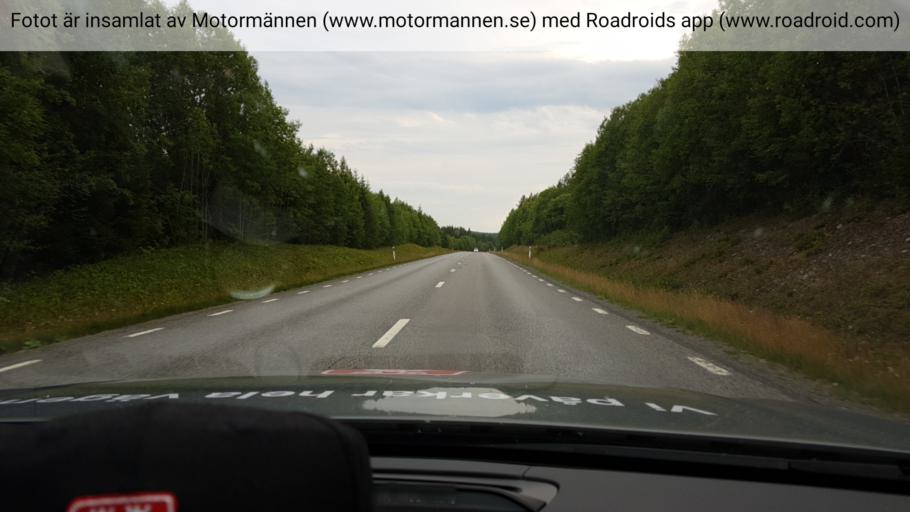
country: SE
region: Jaemtland
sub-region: OEstersunds Kommun
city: Lit
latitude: 63.4571
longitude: 15.1742
